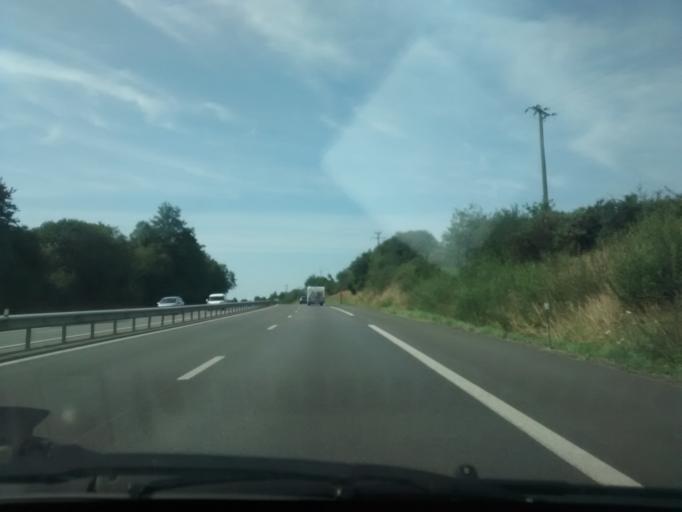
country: FR
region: Brittany
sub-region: Departement des Cotes-d'Armor
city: Broons
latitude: 48.3104
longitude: -2.2390
